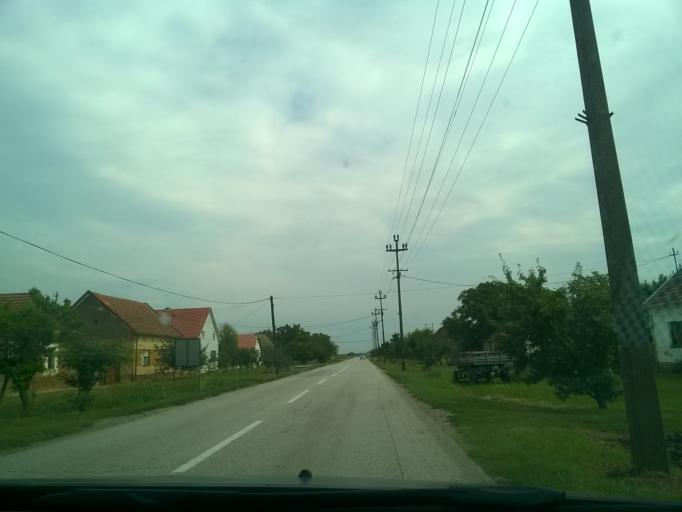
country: RS
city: Sutjeska
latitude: 45.3806
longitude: 20.7010
